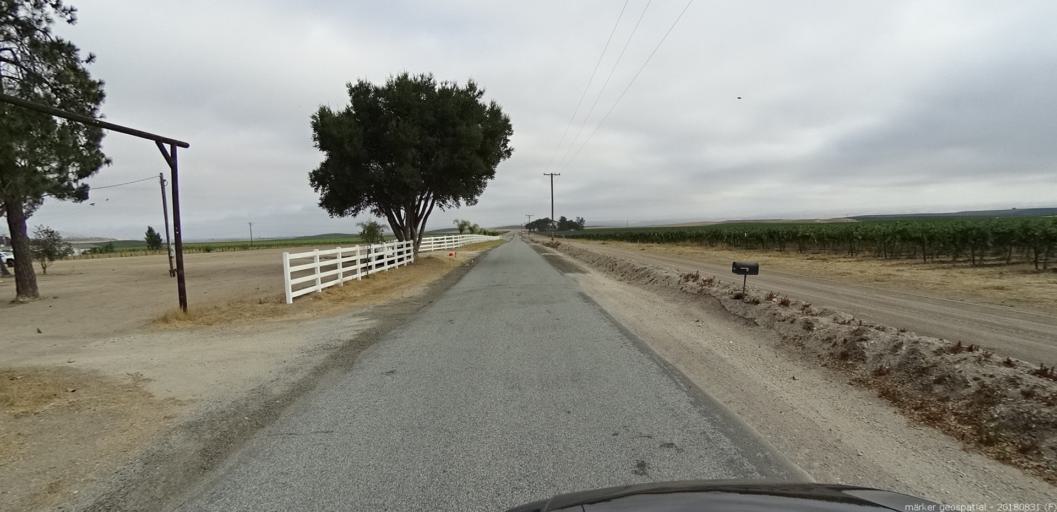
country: US
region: California
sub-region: Monterey County
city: King City
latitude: 36.1414
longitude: -121.1006
